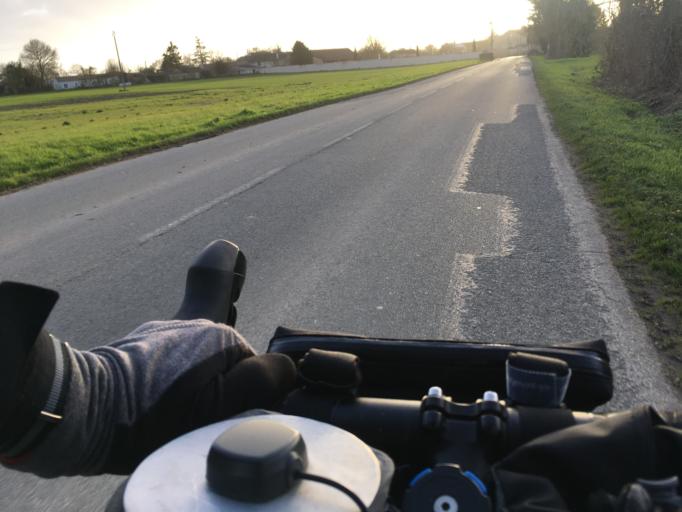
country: FR
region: Poitou-Charentes
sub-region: Departement de la Charente-Maritime
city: Courcon
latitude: 46.1663
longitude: -0.8545
